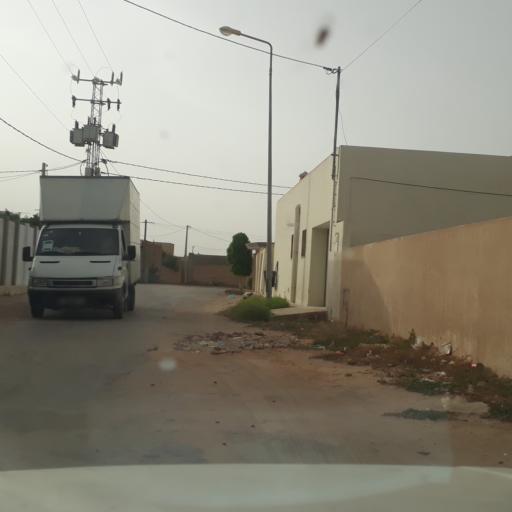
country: TN
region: Safaqis
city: Al Qarmadah
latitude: 34.8156
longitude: 10.7680
